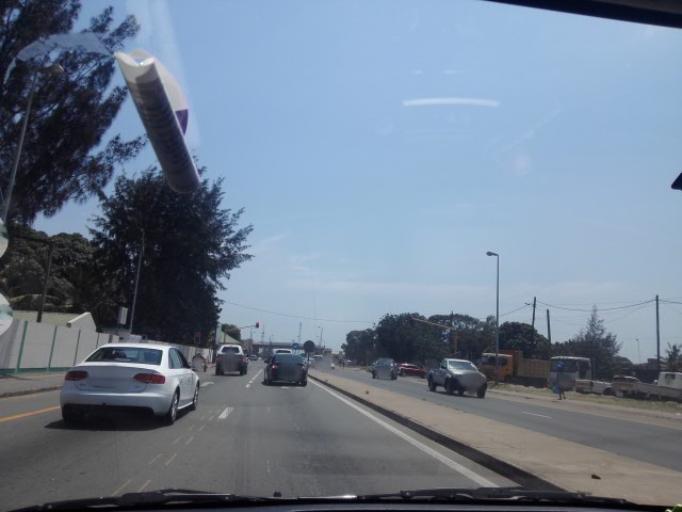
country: MZ
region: Maputo City
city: Maputo
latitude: -25.9417
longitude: 32.5436
